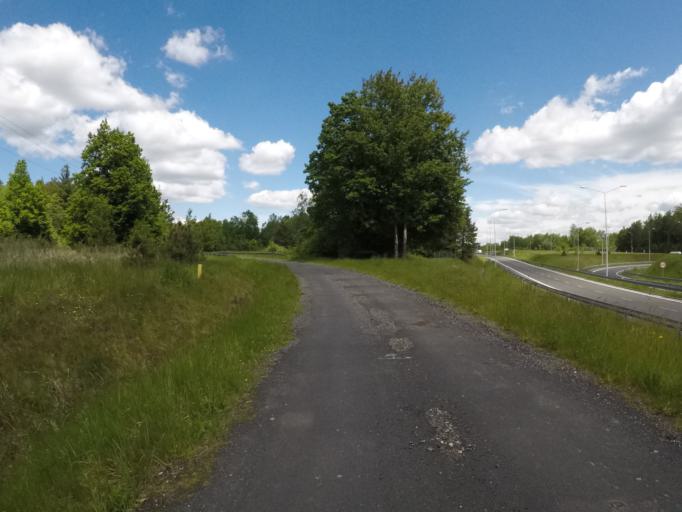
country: PL
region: Swietokrzyskie
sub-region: Powiat kielecki
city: Zagnansk
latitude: 50.9405
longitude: 20.6708
